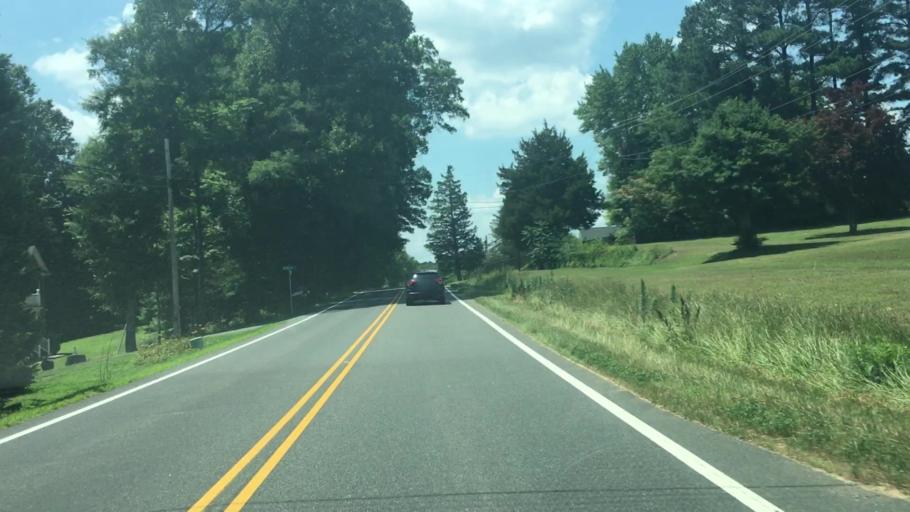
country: US
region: Virginia
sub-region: King George County
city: Passapatanzy
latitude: 38.3026
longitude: -77.3838
